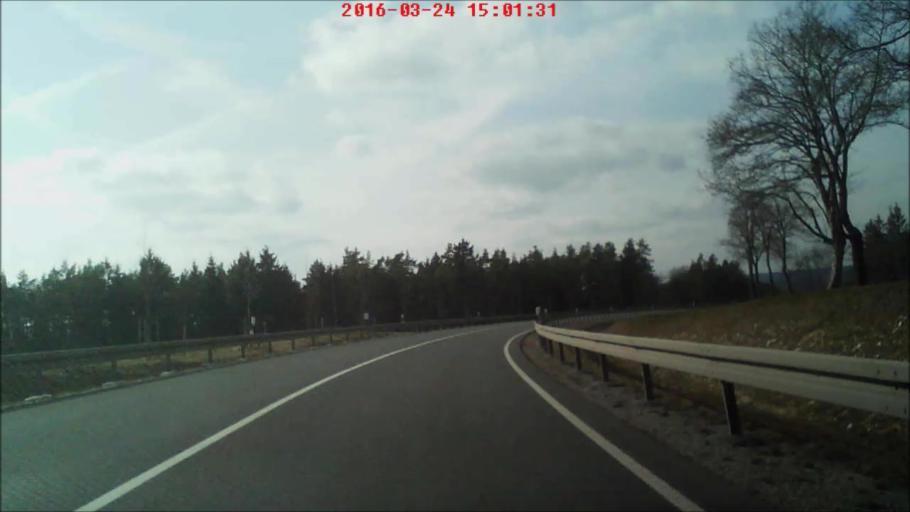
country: DE
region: Thuringia
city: Bad Blankenburg
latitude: 50.7290
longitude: 11.2263
